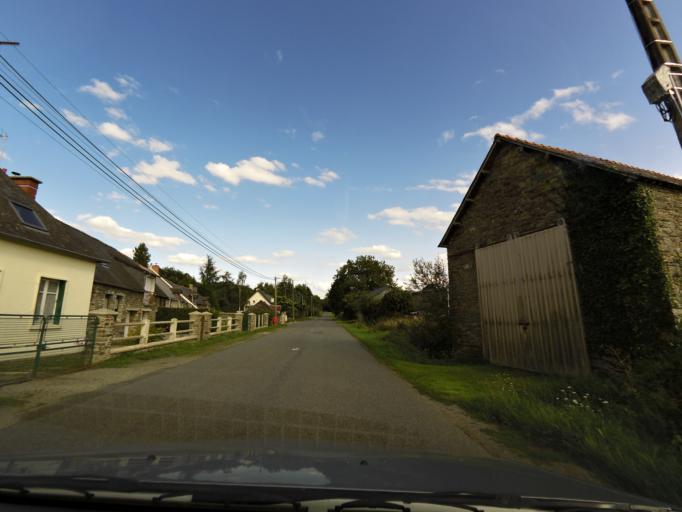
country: FR
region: Brittany
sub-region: Departement d'Ille-et-Vilaine
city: Guignen
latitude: 47.9159
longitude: -1.8288
